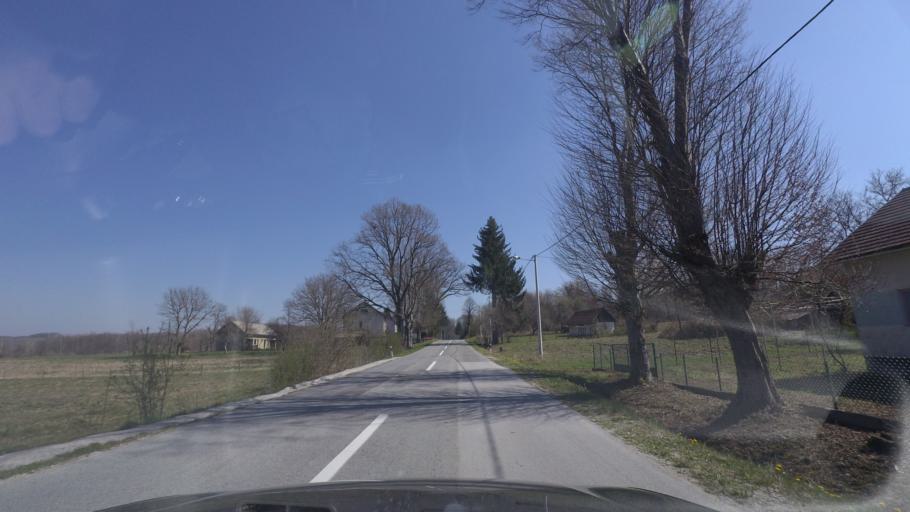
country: HR
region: Sisacko-Moslavacka
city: Gvozd
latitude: 45.3469
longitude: 15.8743
